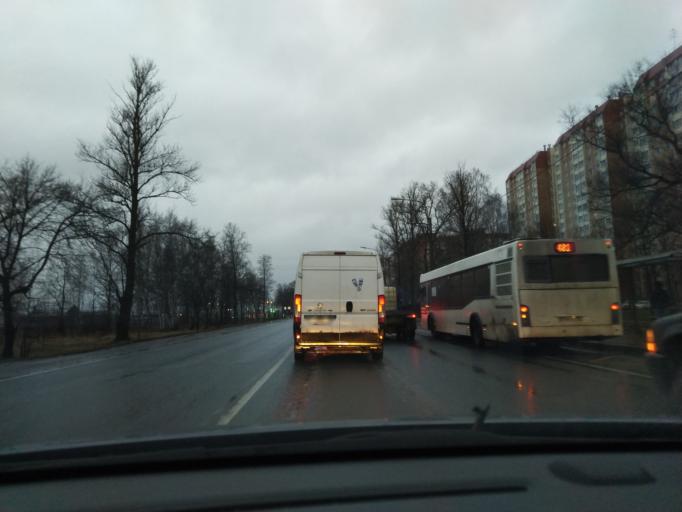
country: RU
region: St.-Petersburg
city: Gorelovo
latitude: 59.7893
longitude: 30.1442
